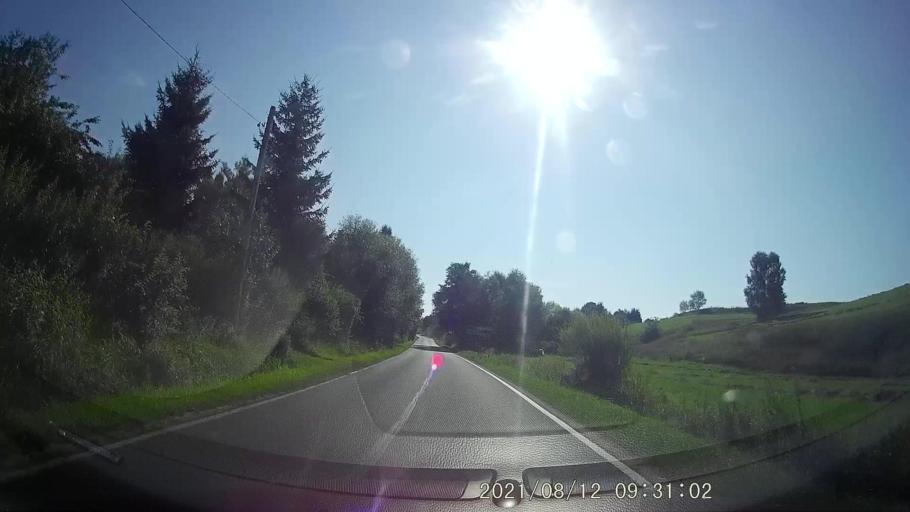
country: PL
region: Lower Silesian Voivodeship
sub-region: Powiat klodzki
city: Radkow
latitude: 50.4882
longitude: 16.4605
